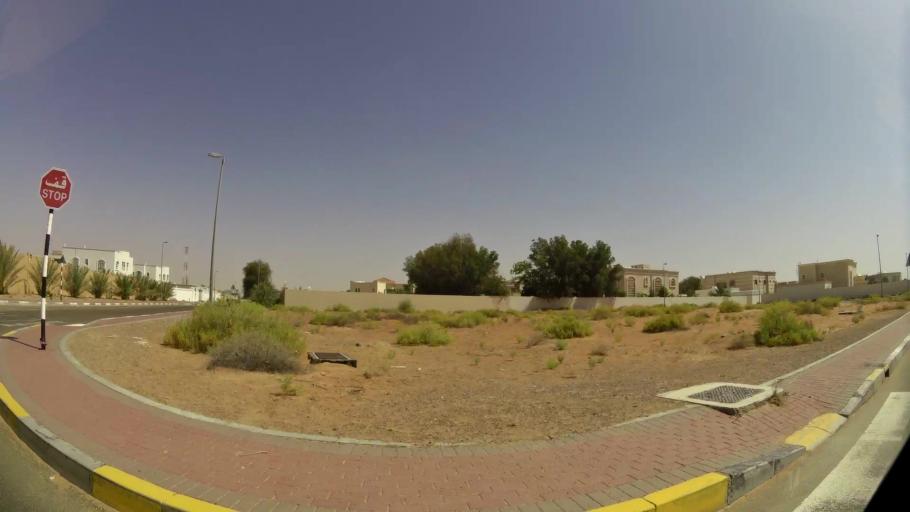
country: OM
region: Al Buraimi
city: Al Buraymi
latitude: 24.2976
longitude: 55.7534
